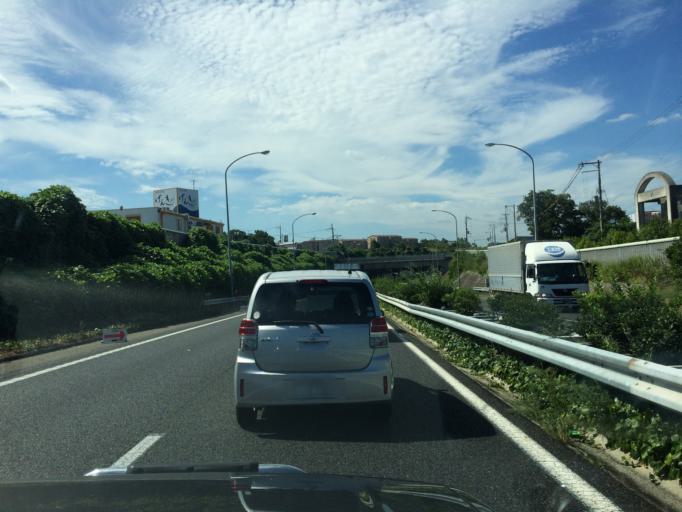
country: JP
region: Osaka
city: Takaishi
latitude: 34.5016
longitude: 135.4876
